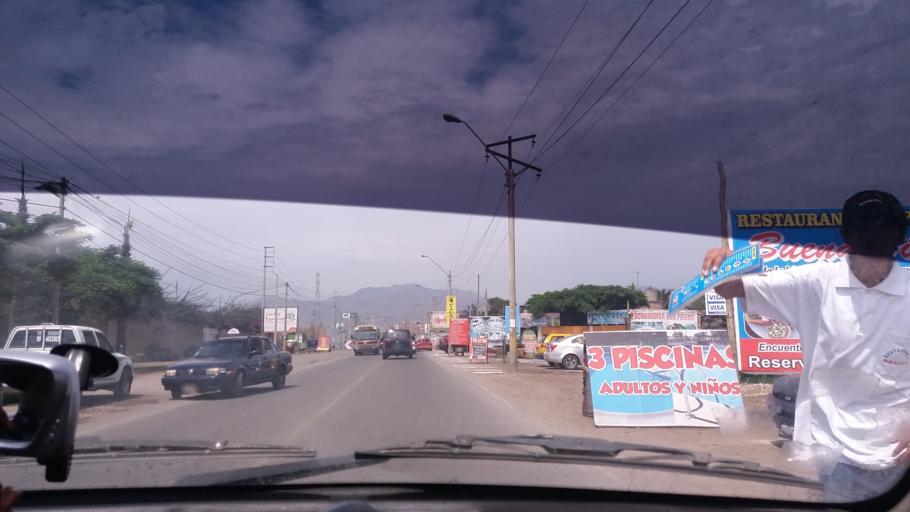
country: PE
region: Lima
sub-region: Lima
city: Punta Hermosa
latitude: -12.2511
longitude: -76.8750
